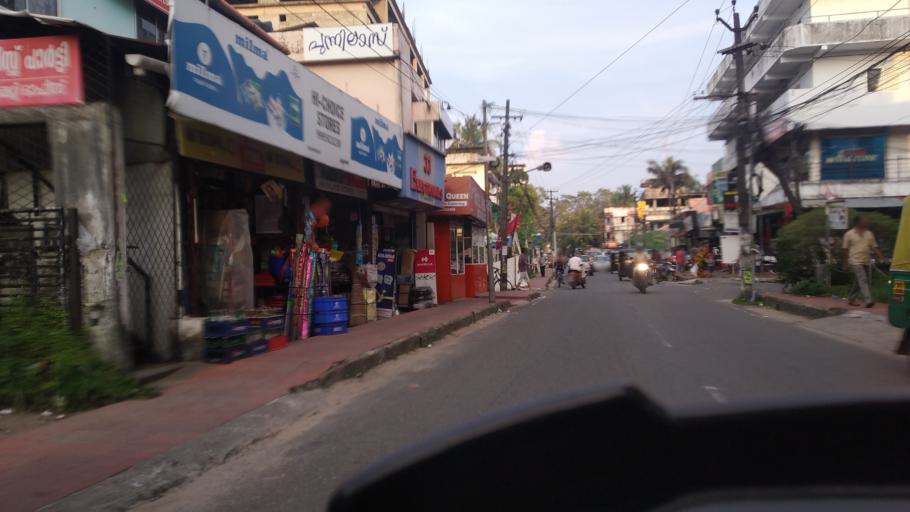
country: IN
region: Kerala
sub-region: Ernakulam
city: Elur
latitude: 10.0190
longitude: 76.2891
